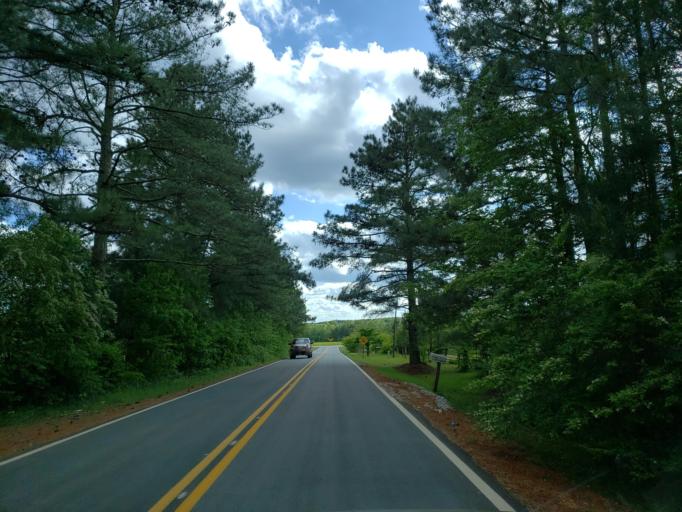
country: US
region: Georgia
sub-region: Carroll County
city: Mount Zion
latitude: 33.6686
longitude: -85.2486
